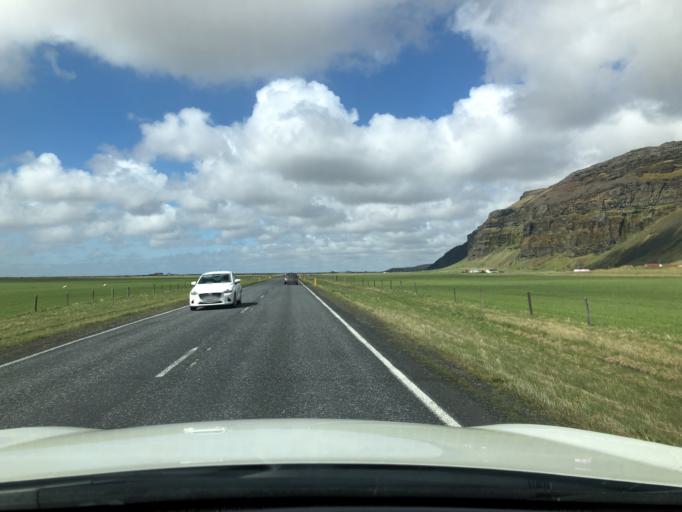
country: IS
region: South
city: Vestmannaeyjar
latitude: 63.5849
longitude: -19.9368
